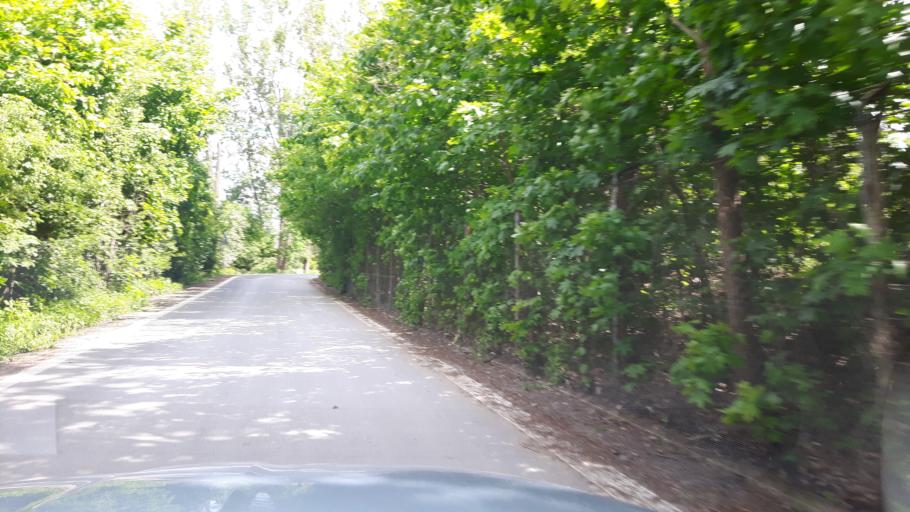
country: PL
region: Masovian Voivodeship
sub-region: Powiat legionowski
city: Stanislawow Pierwszy
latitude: 52.3386
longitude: 21.0335
